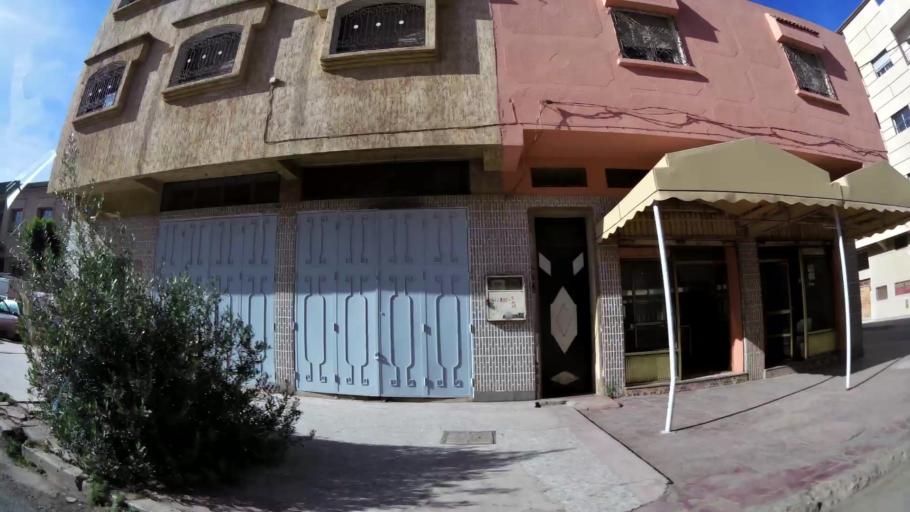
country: MA
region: Oriental
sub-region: Oujda-Angad
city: Oujda
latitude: 34.6756
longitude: -1.8974
